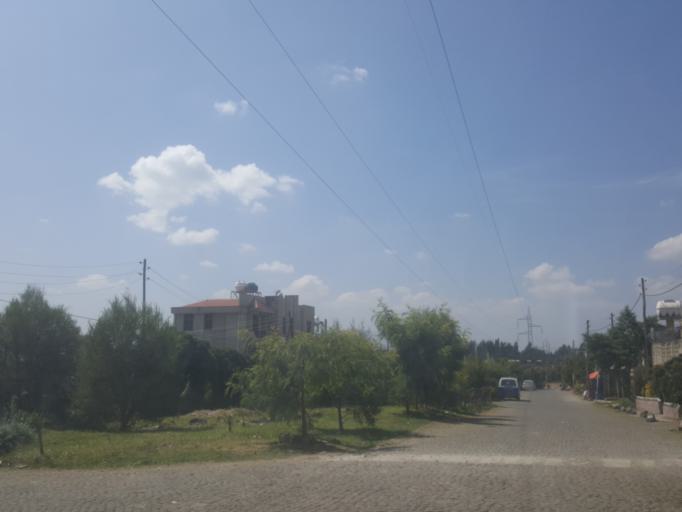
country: ET
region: Adis Abeba
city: Addis Ababa
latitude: 9.0680
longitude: 38.7199
